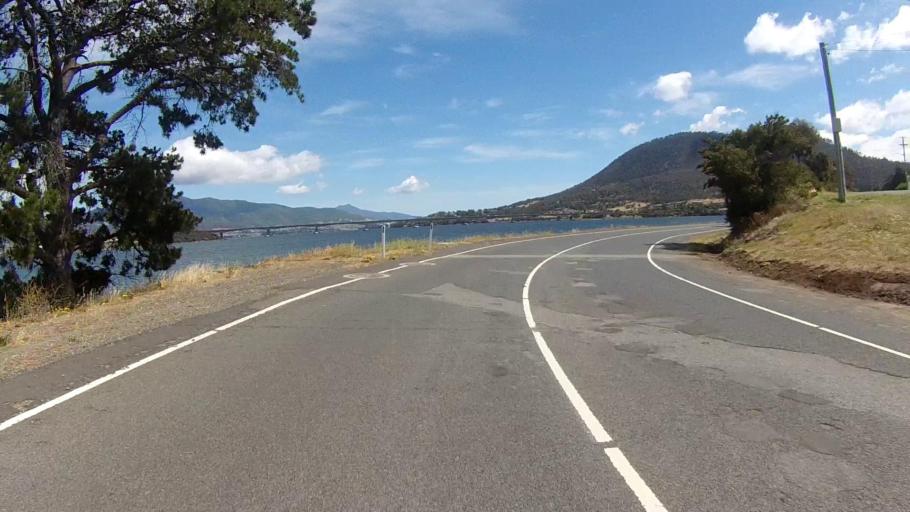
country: AU
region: Tasmania
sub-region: Glenorchy
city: Lutana
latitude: -42.8247
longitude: 147.3182
